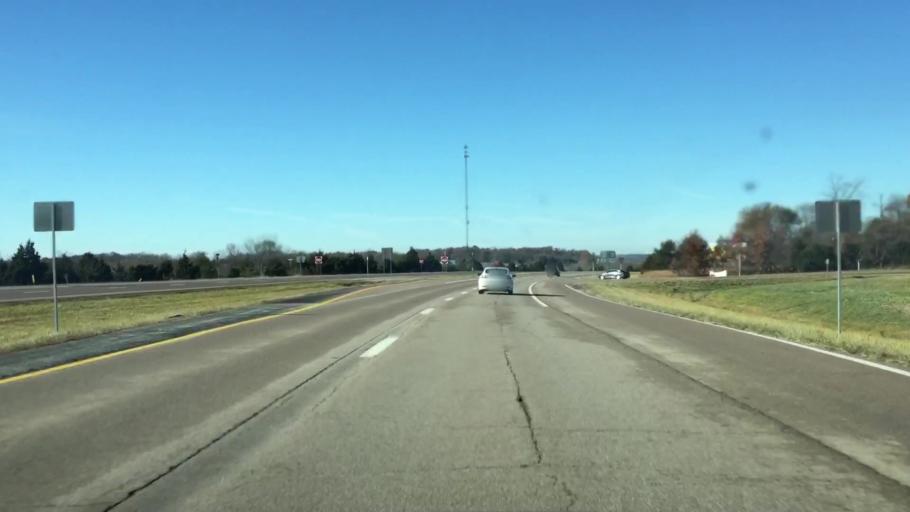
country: US
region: Missouri
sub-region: Miller County
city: Tuscumbia
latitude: 38.3744
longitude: -92.4119
